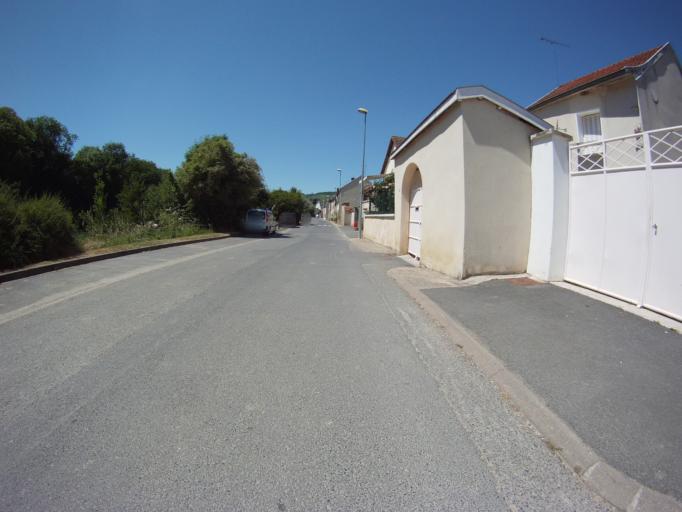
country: FR
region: Champagne-Ardenne
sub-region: Departement de la Marne
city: Damery
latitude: 49.0707
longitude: 3.8762
